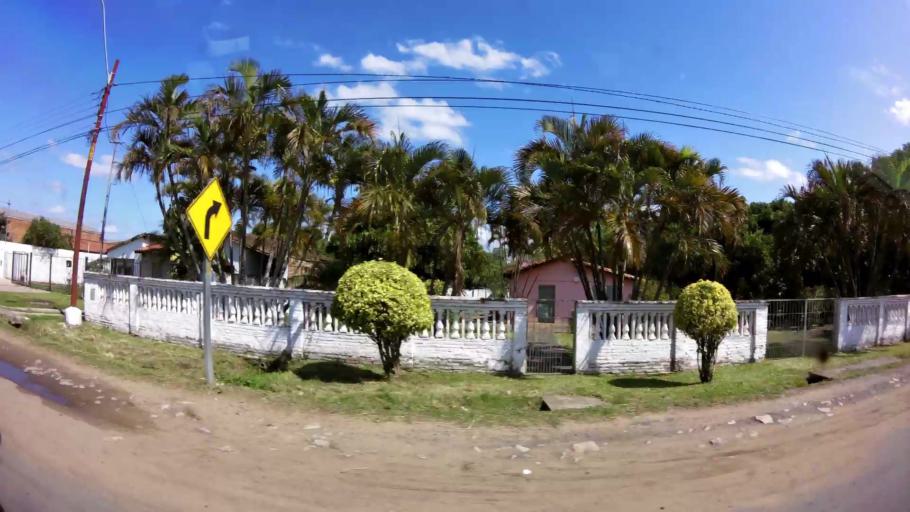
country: PY
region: Central
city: Fernando de la Mora
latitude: -25.2801
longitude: -57.5306
